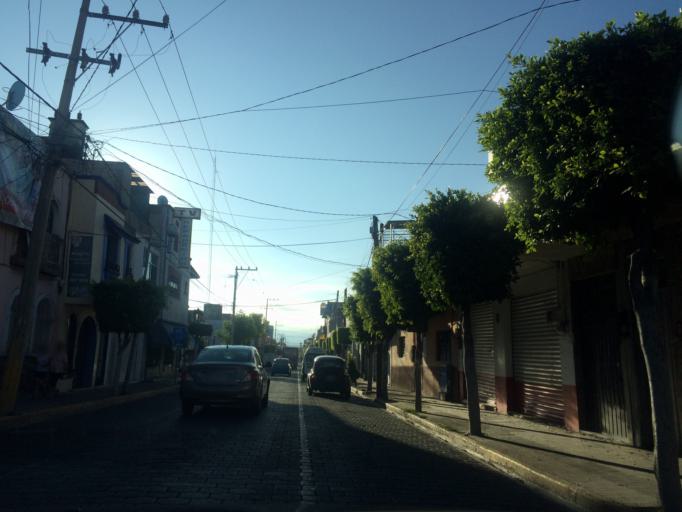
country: MX
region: Puebla
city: Tehuacan
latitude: 18.4632
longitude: -97.3997
